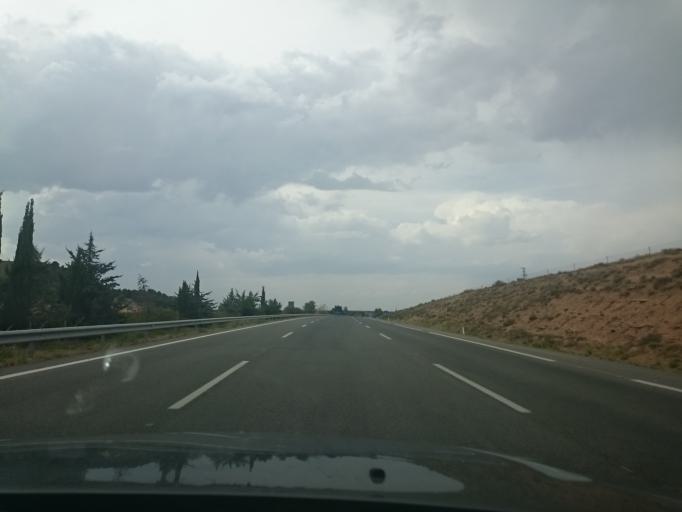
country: ES
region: Navarre
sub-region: Provincia de Navarra
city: Corella
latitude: 42.0864
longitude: -1.7141
